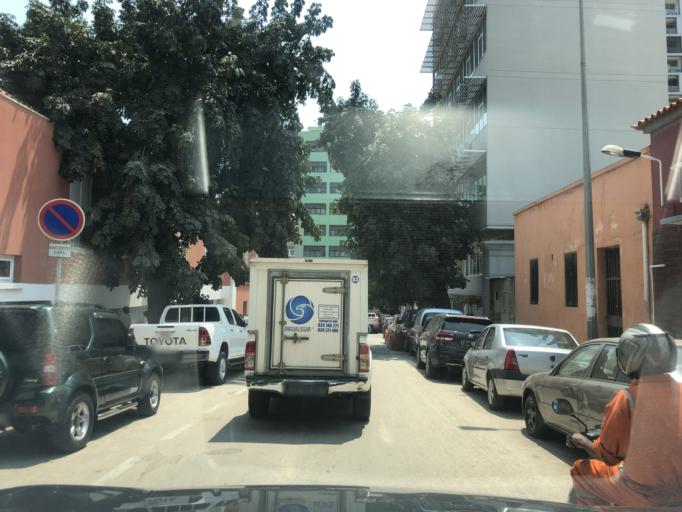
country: AO
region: Luanda
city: Luanda
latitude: -8.8176
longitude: 13.2363
